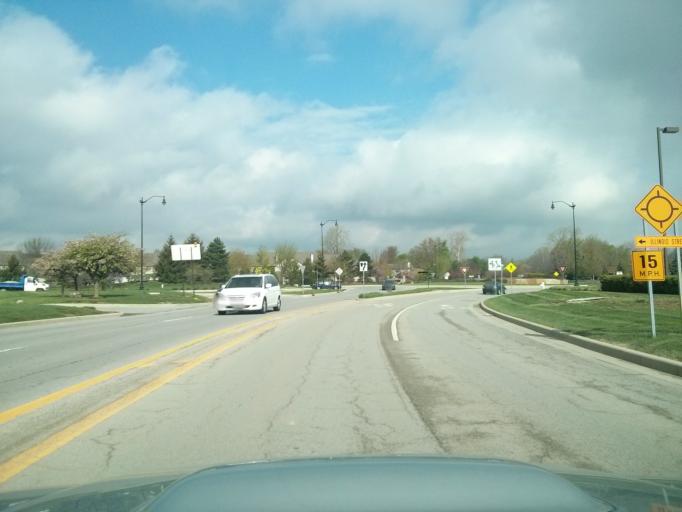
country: US
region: Indiana
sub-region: Hamilton County
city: Carmel
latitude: 39.9713
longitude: -86.1594
